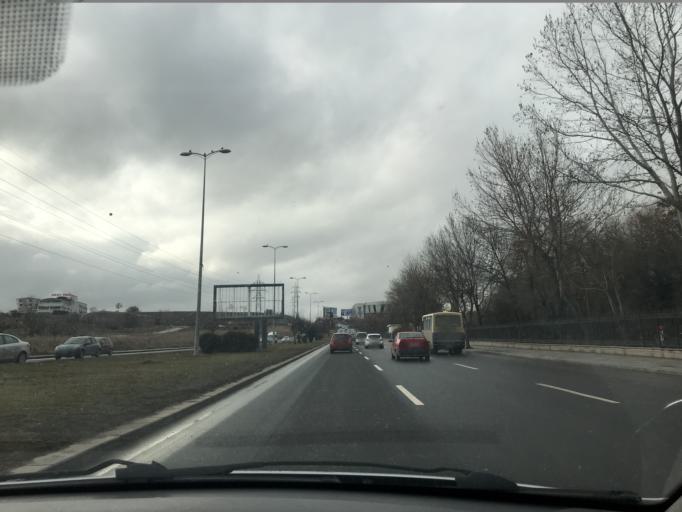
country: TR
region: Ankara
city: Batikent
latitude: 39.9589
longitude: 32.7867
